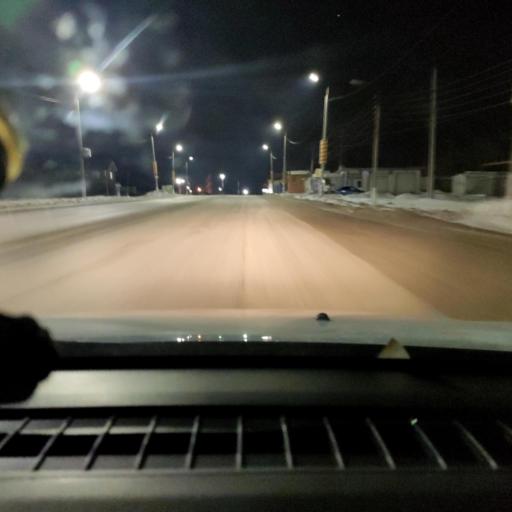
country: RU
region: Samara
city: Novokuybyshevsk
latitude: 53.0801
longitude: 49.9612
